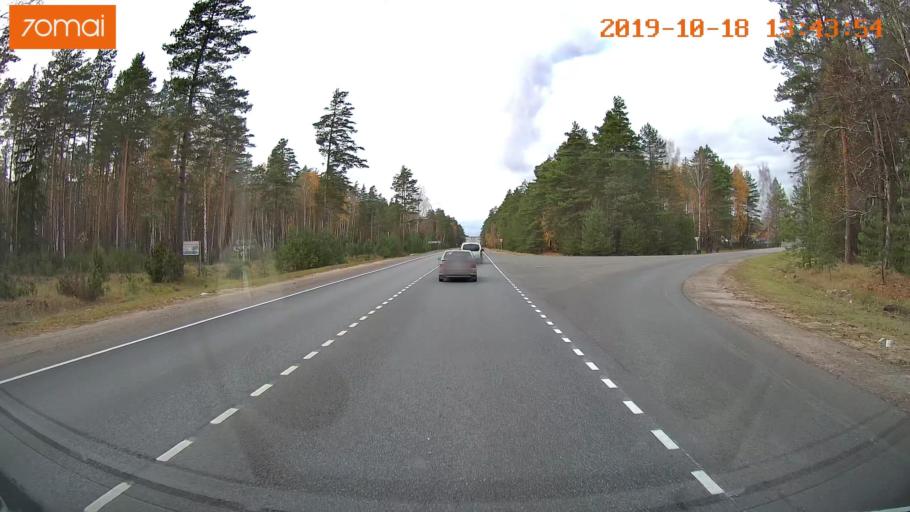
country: RU
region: Rjazan
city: Solotcha
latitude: 54.9334
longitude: 39.9704
